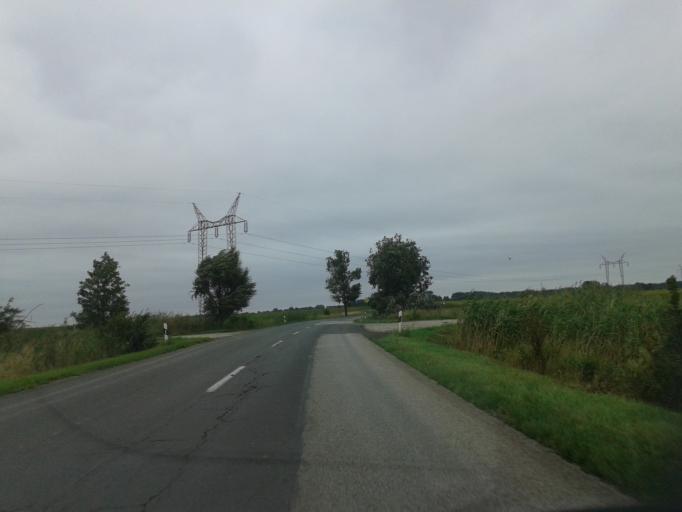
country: HU
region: Bacs-Kiskun
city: Tass
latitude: 47.0459
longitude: 19.0231
